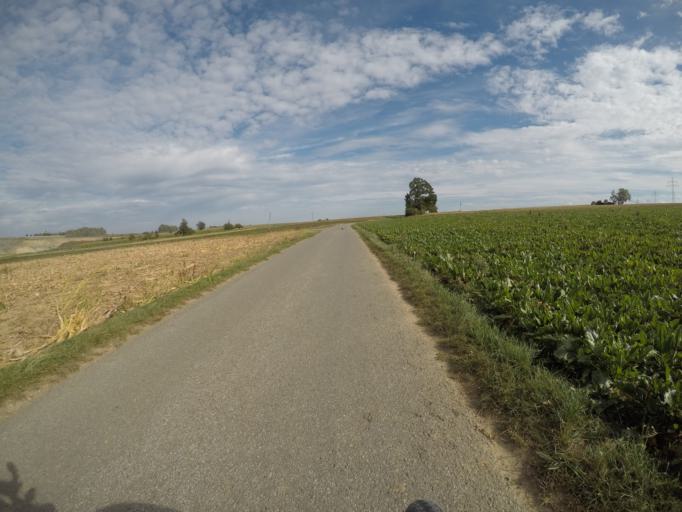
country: DE
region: Baden-Wuerttemberg
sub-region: Regierungsbezirk Stuttgart
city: Leonberg
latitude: 48.8327
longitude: 9.0005
